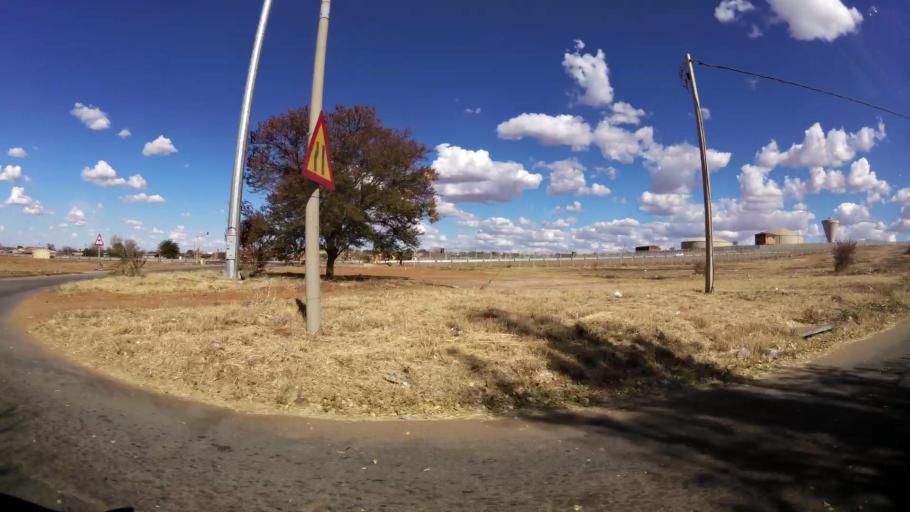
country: ZA
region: North-West
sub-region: Dr Kenneth Kaunda District Municipality
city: Klerksdorp
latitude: -26.8738
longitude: 26.5976
